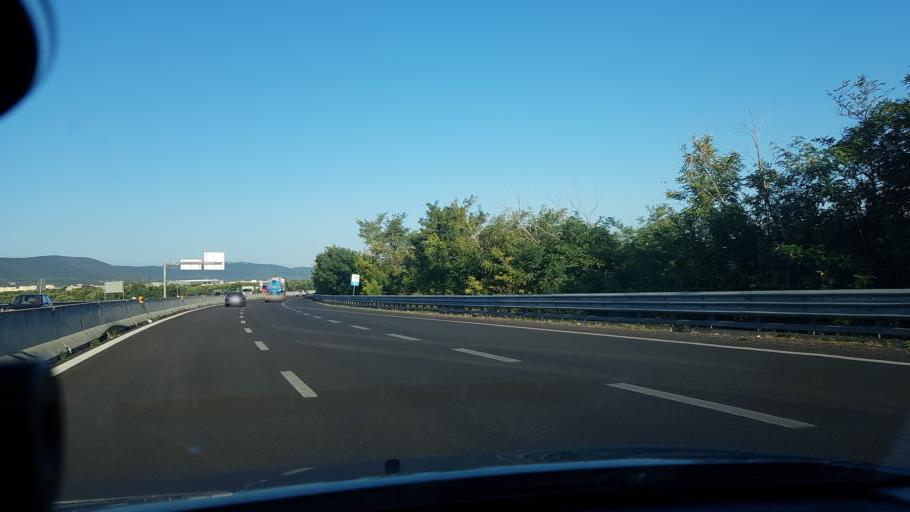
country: IT
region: Apulia
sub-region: Provincia di Brindisi
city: Fasano
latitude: 40.8415
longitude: 17.3690
